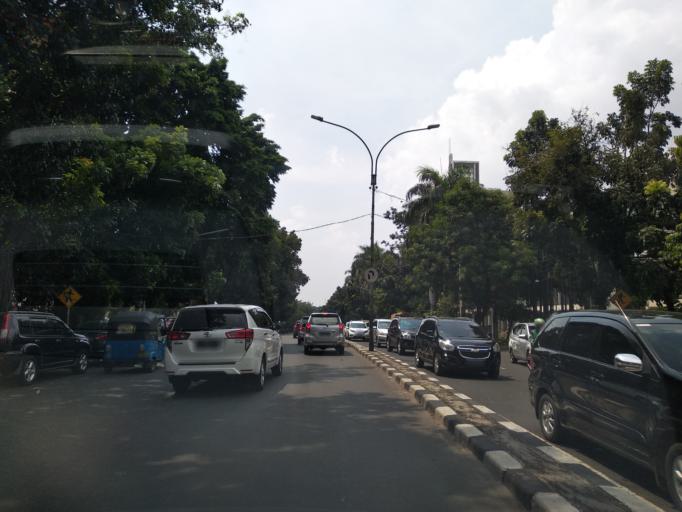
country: ID
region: Jakarta Raya
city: Jakarta
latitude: -6.2270
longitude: 106.8475
